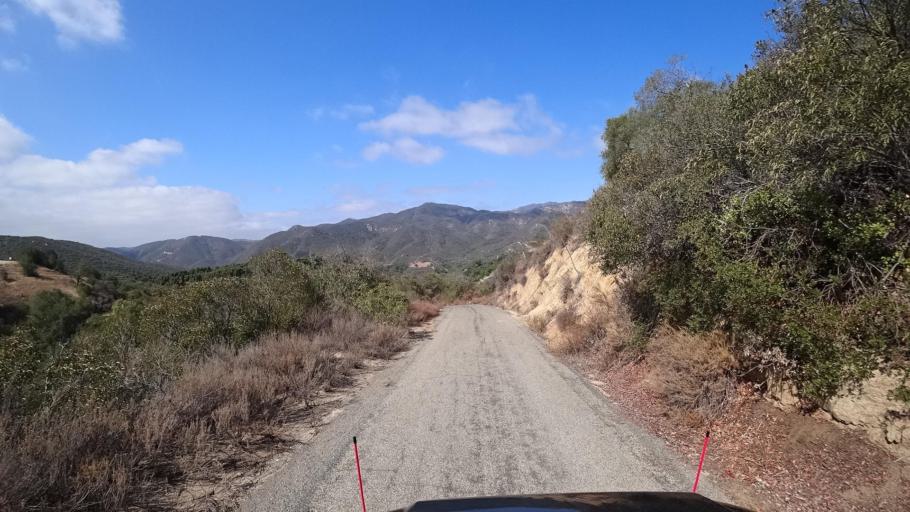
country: US
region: California
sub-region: San Diego County
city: Fallbrook
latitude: 33.4220
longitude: -117.3117
